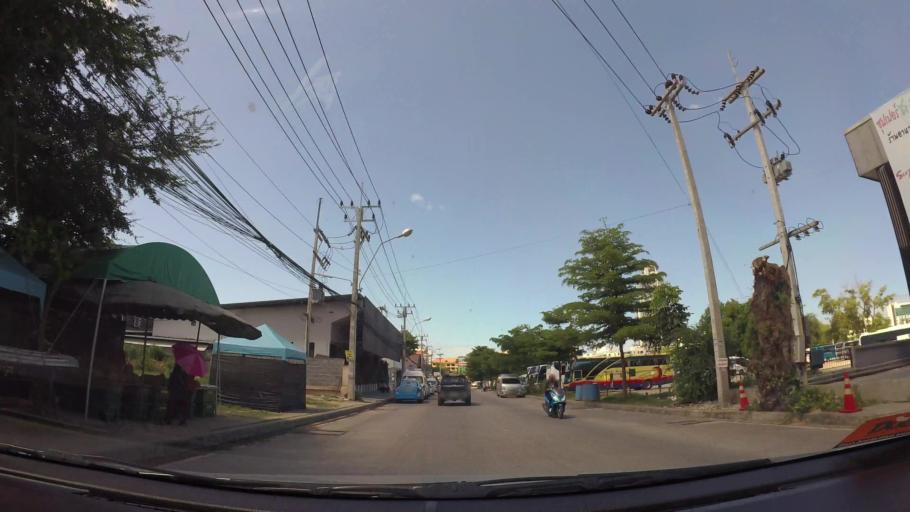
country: TH
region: Chon Buri
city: Phatthaya
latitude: 12.9437
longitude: 100.8916
